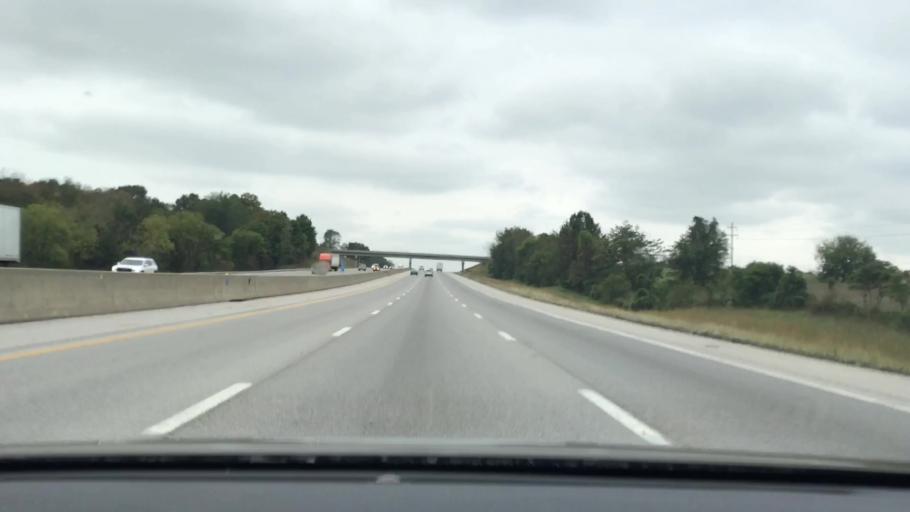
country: US
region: Kentucky
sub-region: Warren County
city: Plano
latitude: 36.7986
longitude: -86.4747
